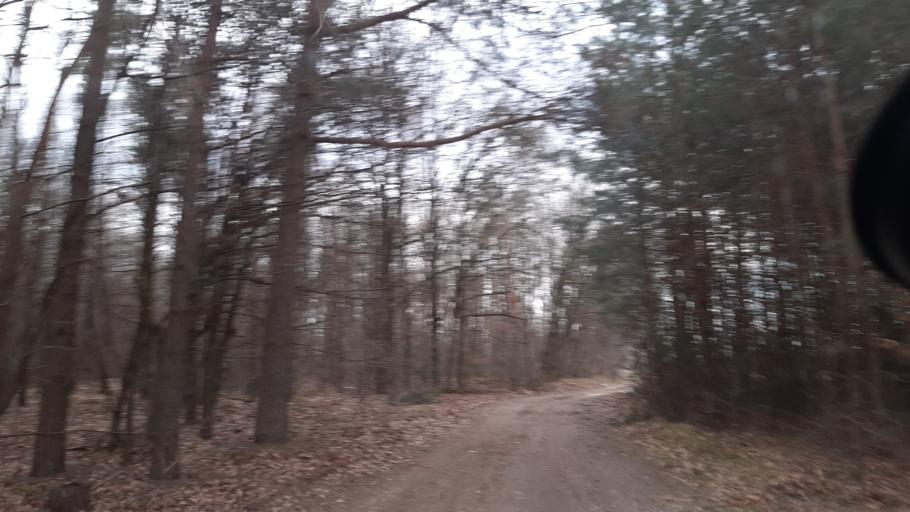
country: PL
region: Lublin Voivodeship
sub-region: Powiat lubelski
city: Garbow
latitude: 51.3967
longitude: 22.4069
